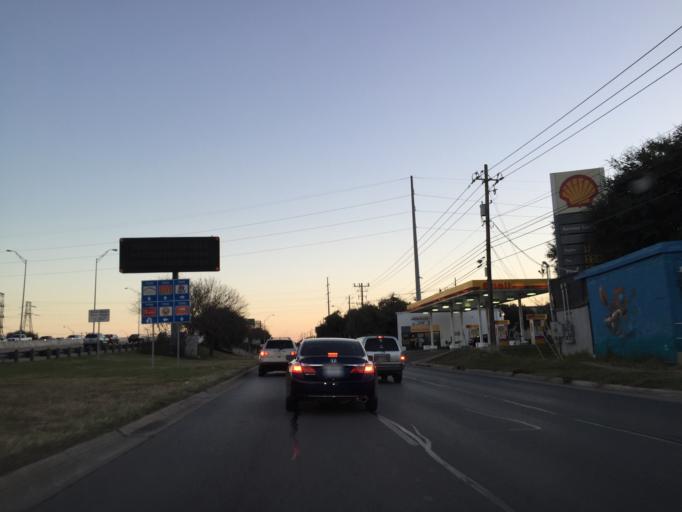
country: US
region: Texas
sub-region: Williamson County
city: Jollyville
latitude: 30.4033
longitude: -97.7460
